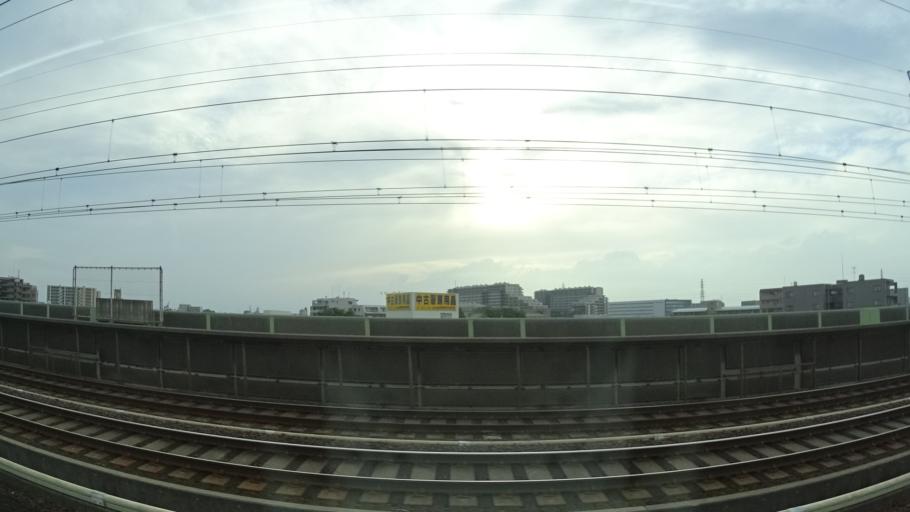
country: JP
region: Saitama
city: Ageoshimo
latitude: 35.9344
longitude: 139.6166
